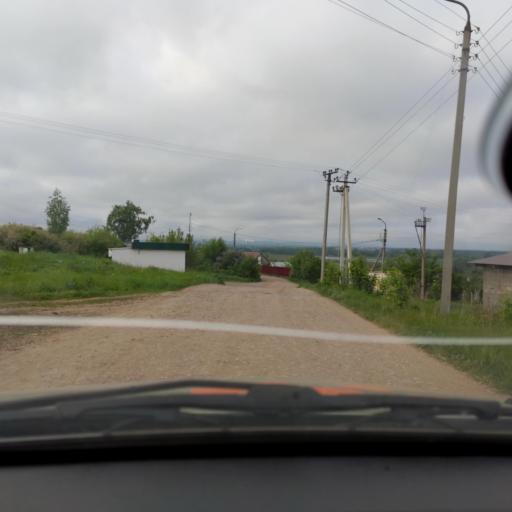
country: RU
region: Bashkortostan
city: Blagoveshchensk
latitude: 54.8918
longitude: 56.0407
